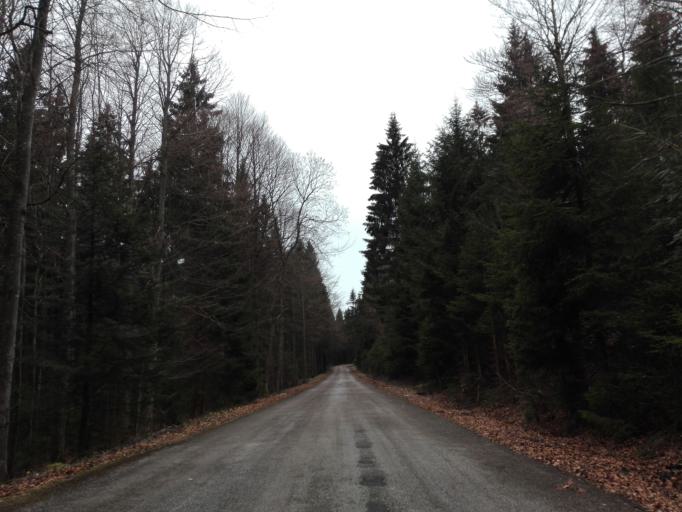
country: AT
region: Upper Austria
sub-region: Politischer Bezirk Rohrbach
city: Aigen im Muehlkreis
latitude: 48.7019
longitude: 13.9720
